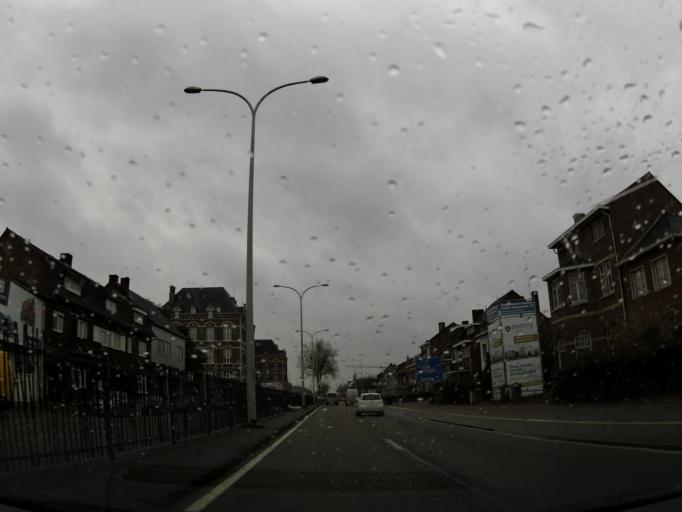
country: BE
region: Flanders
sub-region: Provincie Limburg
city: Maasmechelen
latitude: 50.9689
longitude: 5.6975
